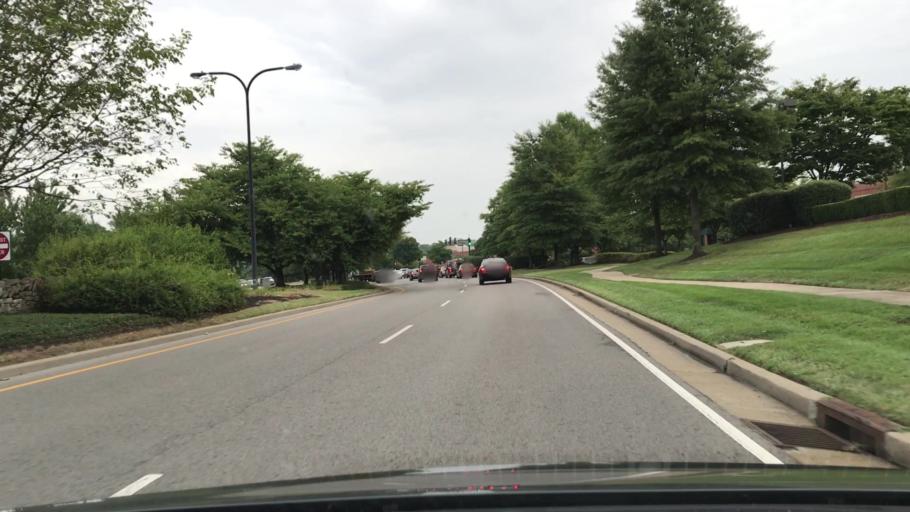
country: US
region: Tennessee
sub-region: Williamson County
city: Brentwood Estates
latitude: 35.9570
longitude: -86.8029
